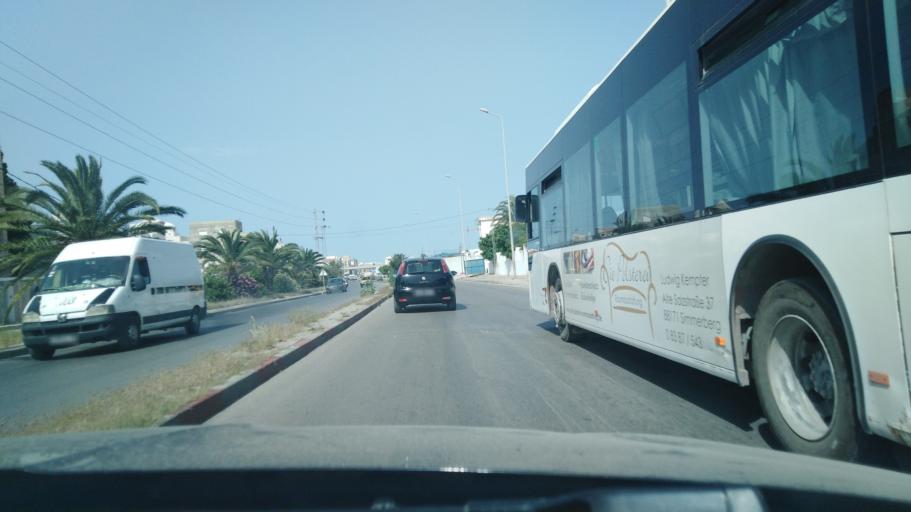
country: TN
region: Susah
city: Sousse
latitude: 35.8000
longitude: 10.6107
